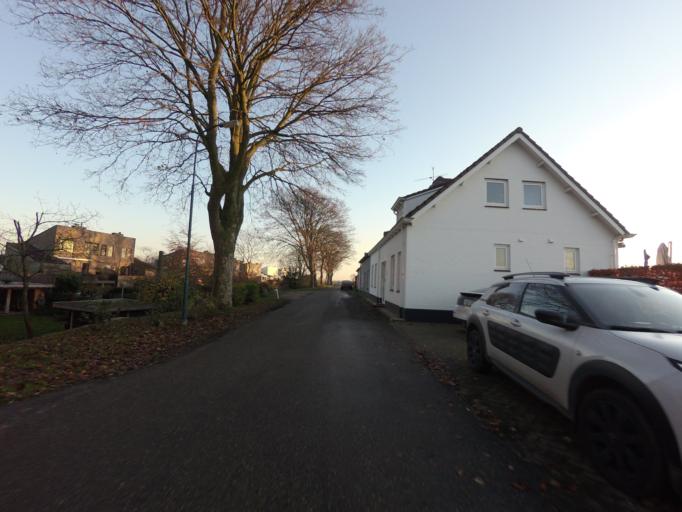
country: NL
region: Gelderland
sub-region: Gemeente Zaltbommel
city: Nederhemert-Noord
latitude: 51.7474
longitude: 5.2116
